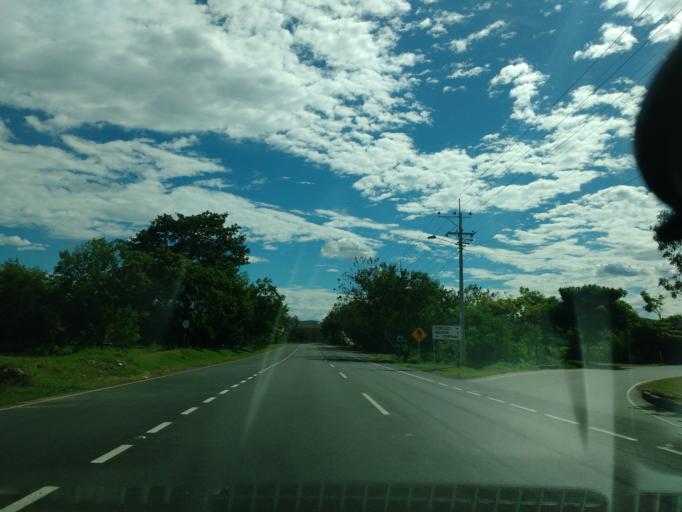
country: CO
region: Tolima
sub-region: Flandes
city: Flandes
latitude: 4.2441
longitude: -74.8853
